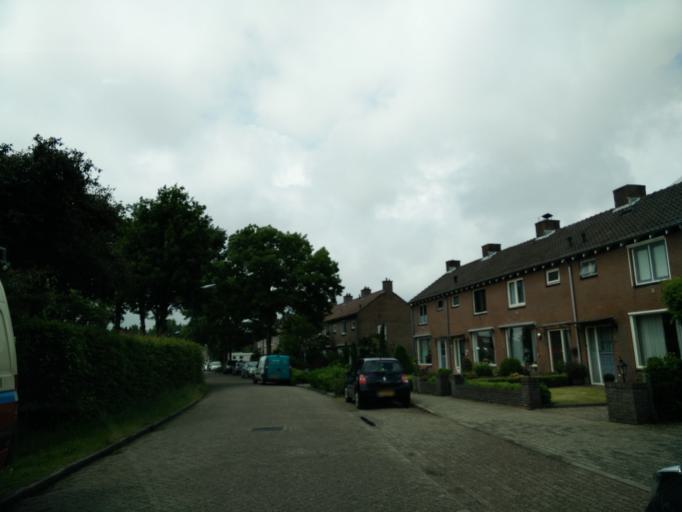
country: NL
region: Utrecht
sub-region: Gemeente Utrechtse Heuvelrug
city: Leersum
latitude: 52.0087
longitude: 5.4344
